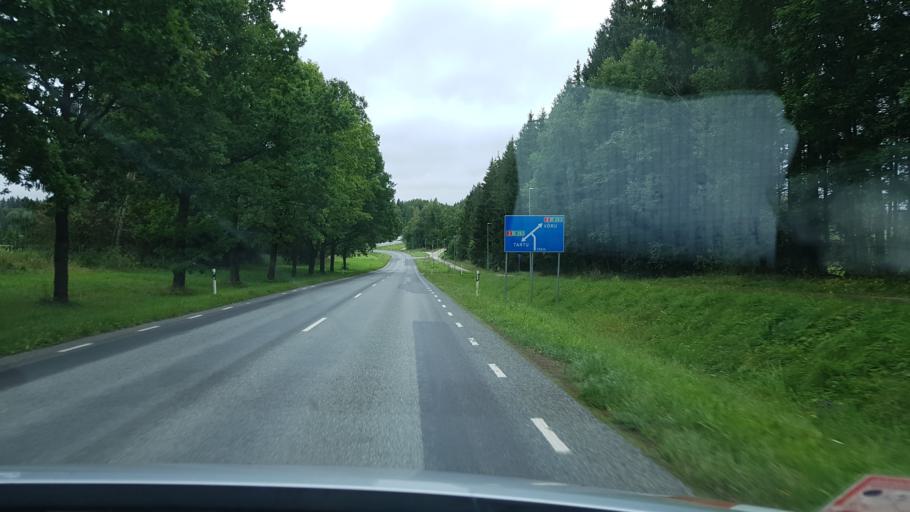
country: EE
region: Vorumaa
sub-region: Antsla vald
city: Vana-Antsla
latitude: 57.9807
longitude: 26.7715
